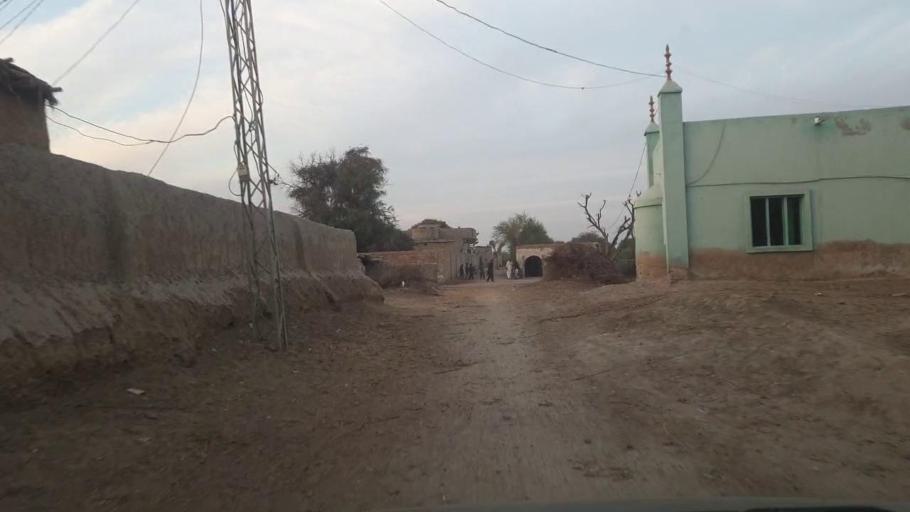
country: PK
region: Sindh
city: Shahpur Chakar
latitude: 26.0689
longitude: 68.5362
